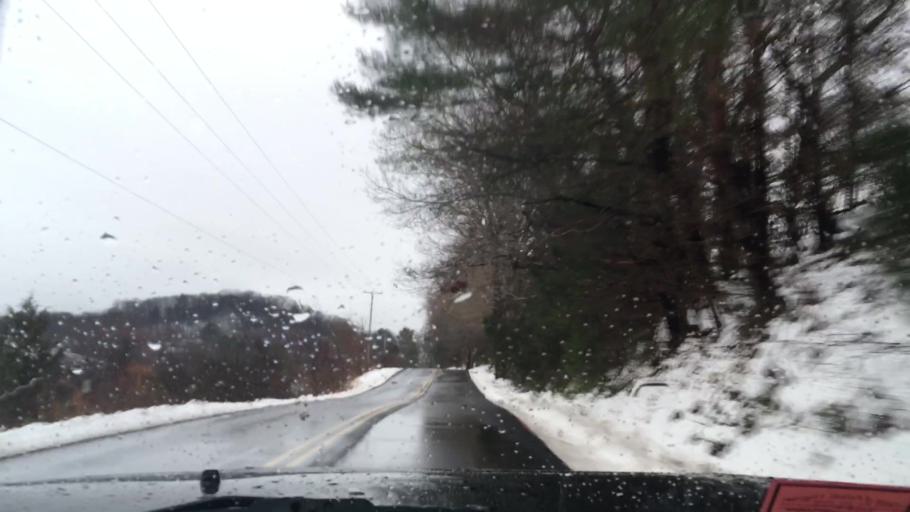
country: US
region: Virginia
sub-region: Pulaski County
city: Dublin
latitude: 37.0179
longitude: -80.6345
